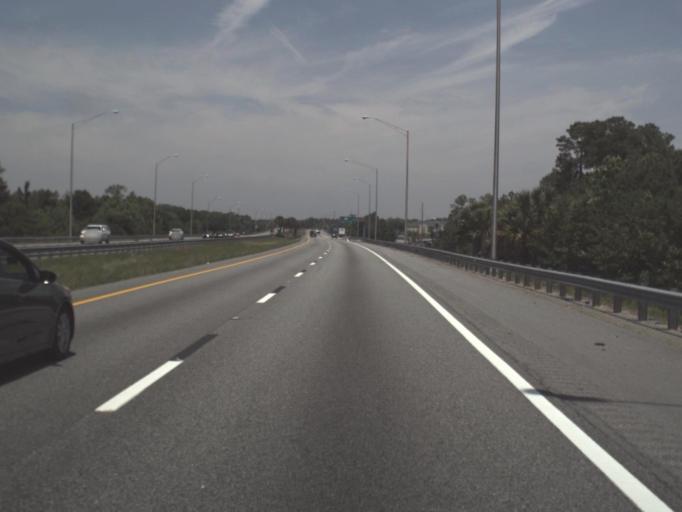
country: US
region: Florida
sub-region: Duval County
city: Atlantic Beach
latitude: 30.3175
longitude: -81.5249
